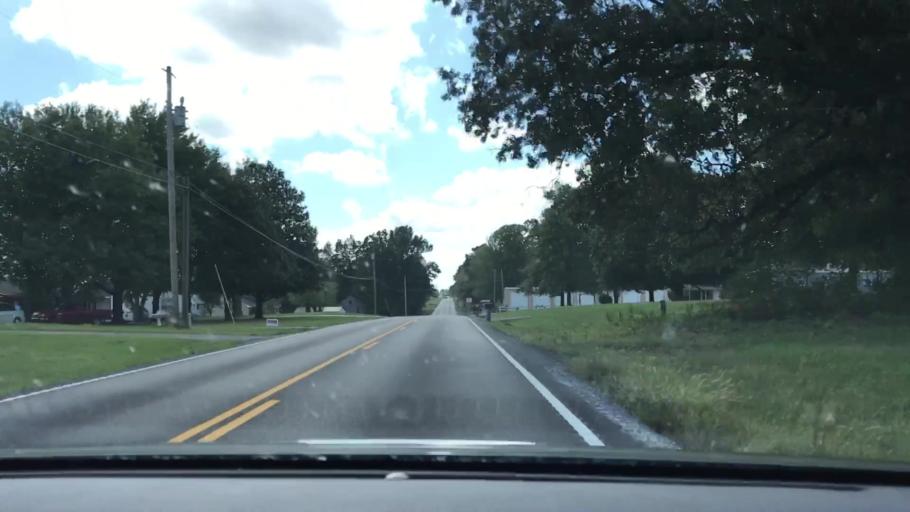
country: US
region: Kentucky
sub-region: Graves County
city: Mayfield
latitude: 36.7709
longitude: -88.5960
